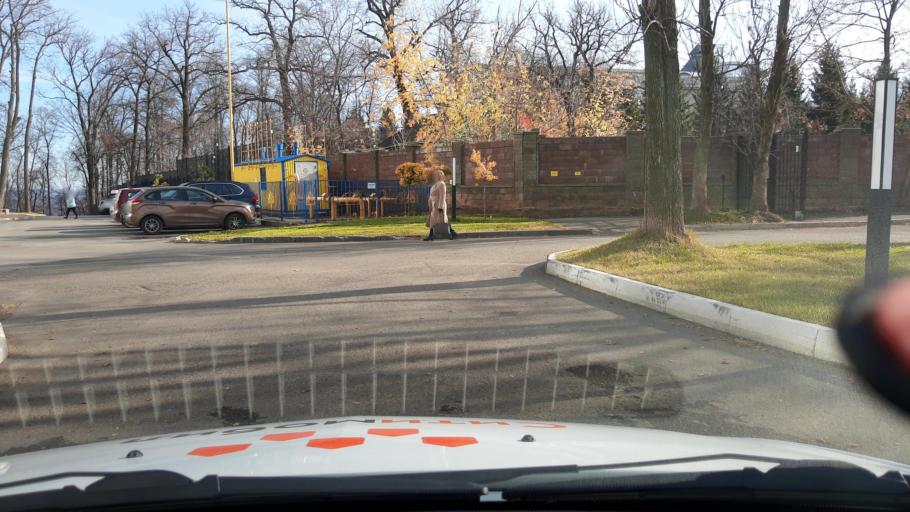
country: RU
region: Bashkortostan
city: Ufa
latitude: 54.7210
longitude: 56.0228
